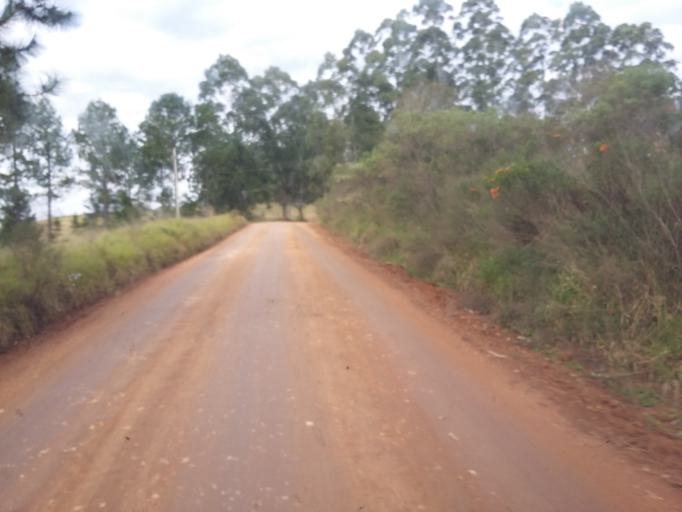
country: BR
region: Rio Grande do Sul
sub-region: Camaqua
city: Camaqua
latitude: -30.7192
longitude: -51.7819
